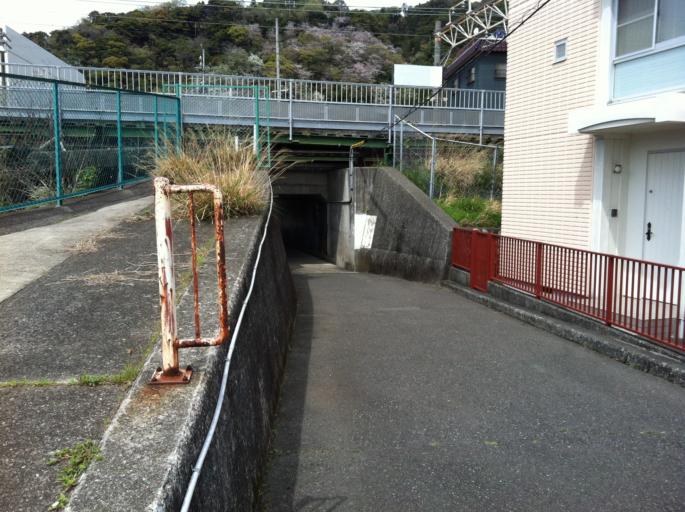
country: JP
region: Shizuoka
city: Fuji
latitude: 35.1189
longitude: 138.6069
